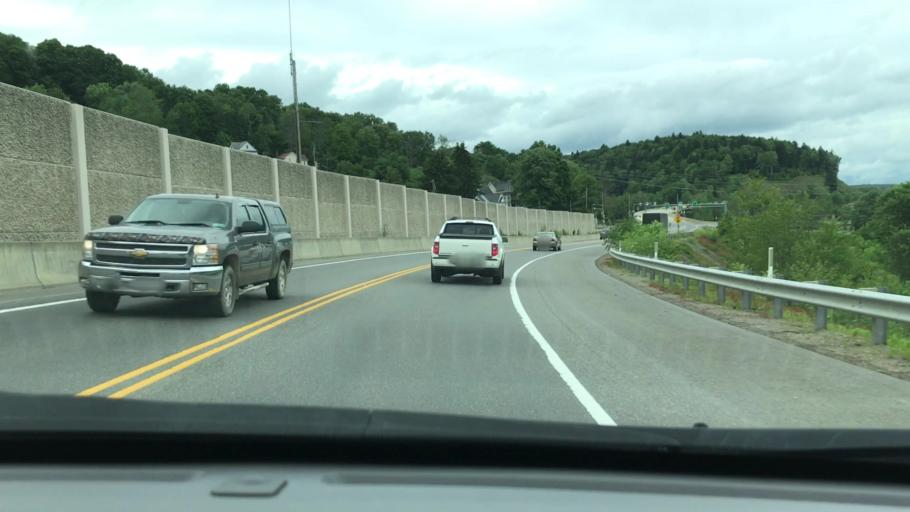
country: US
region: Pennsylvania
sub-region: Elk County
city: Johnsonburg
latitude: 41.4834
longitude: -78.6767
